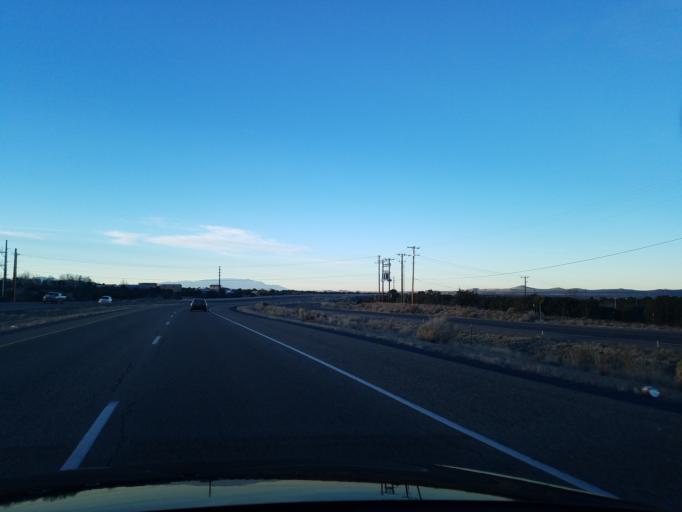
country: US
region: New Mexico
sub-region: Santa Fe County
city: Agua Fria
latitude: 35.6701
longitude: -106.0180
